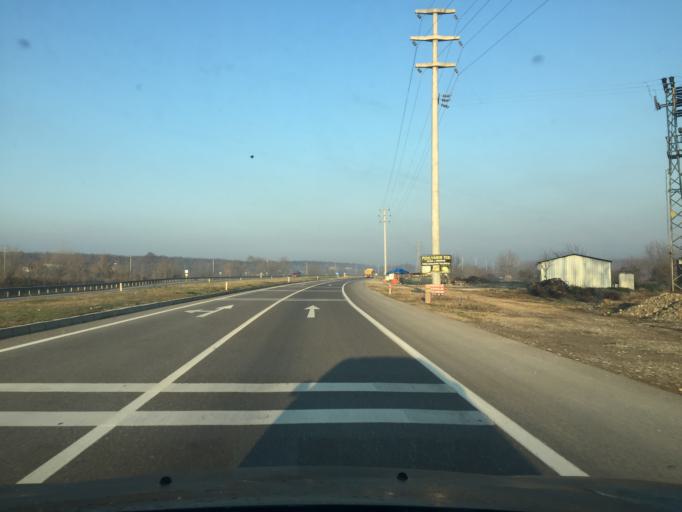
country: TR
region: Sakarya
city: Akyazi
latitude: 40.6480
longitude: 30.6072
